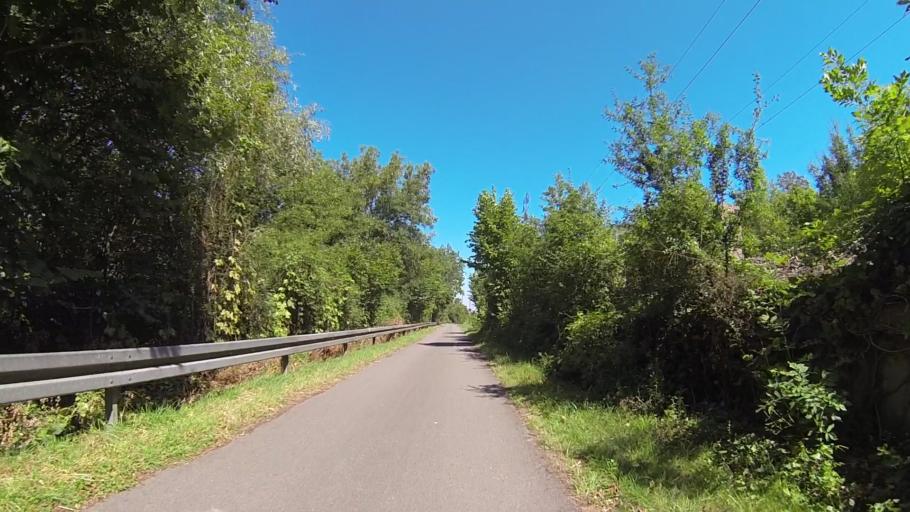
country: LU
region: Grevenmacher
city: Schengen
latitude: 49.4885
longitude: 6.3705
